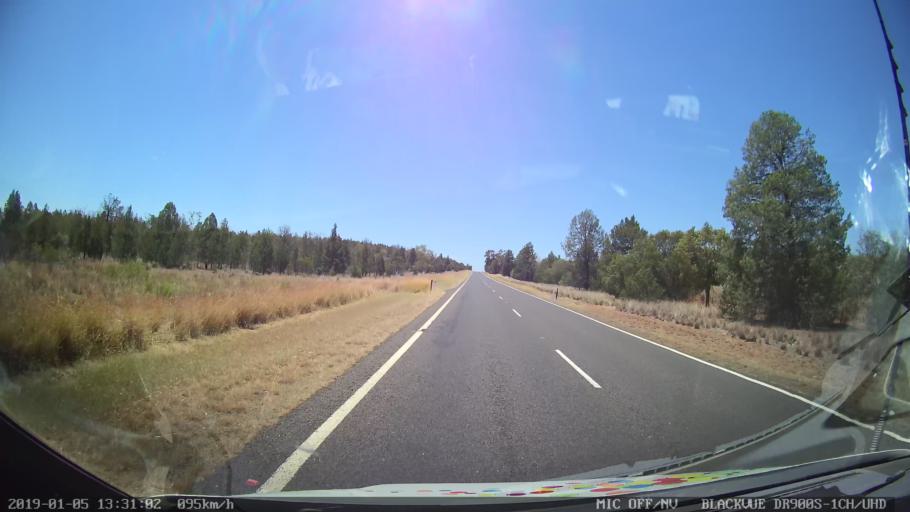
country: AU
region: New South Wales
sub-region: Gunnedah
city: Gunnedah
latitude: -31.0139
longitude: 150.0788
